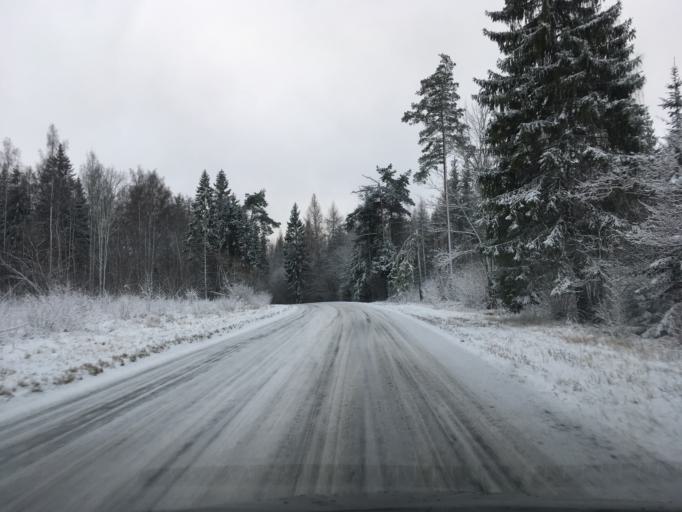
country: EE
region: Harju
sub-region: Raasiku vald
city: Raasiku
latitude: 59.2254
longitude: 25.1822
